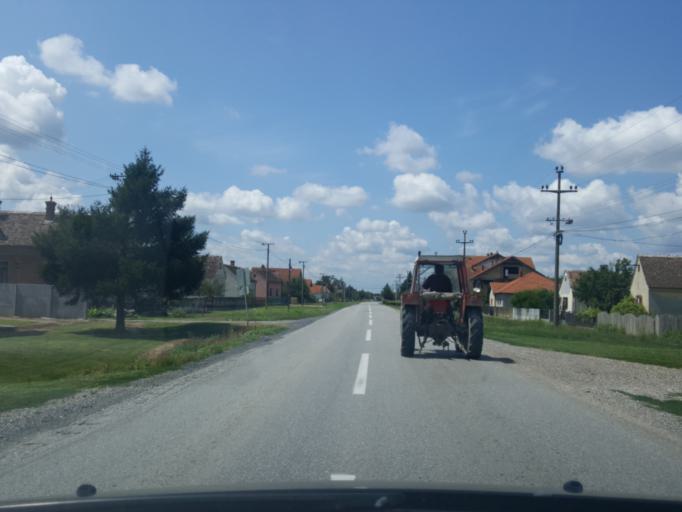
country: RS
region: Central Serbia
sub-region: Macvanski Okrug
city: Bogatic
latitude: 44.8408
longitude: 19.5037
